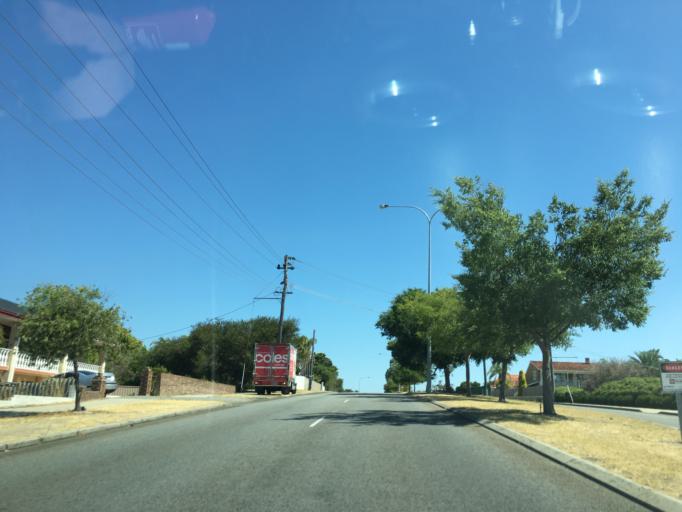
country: AU
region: Western Australia
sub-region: Canning
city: Canning Vale
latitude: -32.0491
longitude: 115.9042
